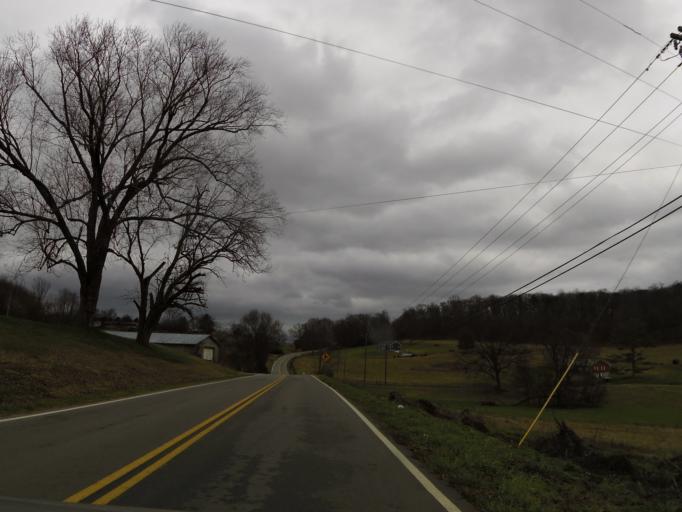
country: US
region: Tennessee
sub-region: Grainger County
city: Rutledge
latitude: 36.2045
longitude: -83.5748
